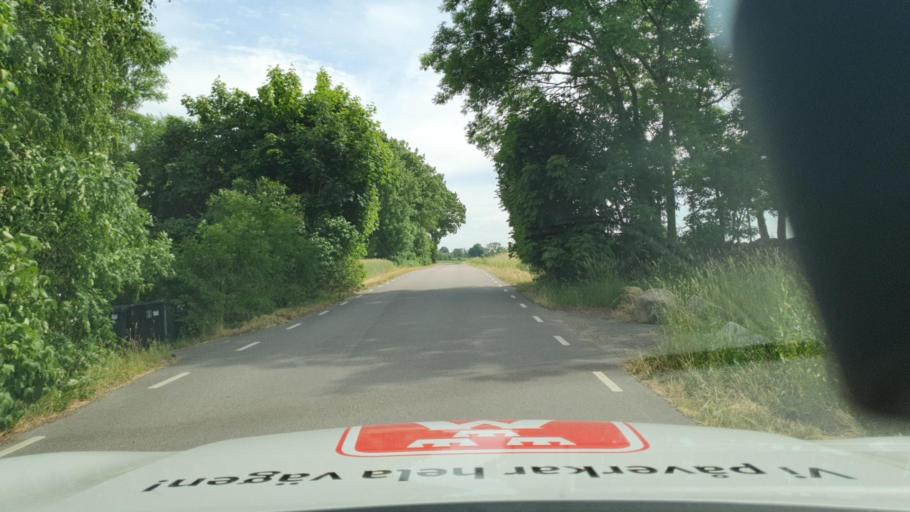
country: SE
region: Skane
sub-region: Tomelilla Kommun
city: Tomelilla
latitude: 55.6623
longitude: 13.9061
